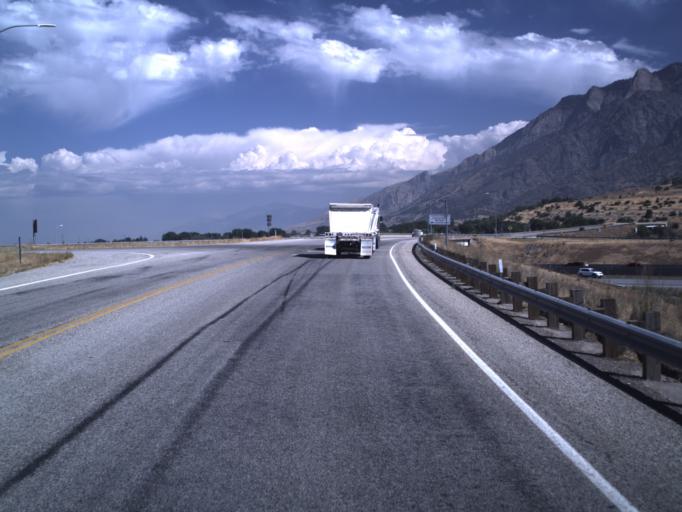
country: US
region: Utah
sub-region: Box Elder County
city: South Willard
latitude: 41.3391
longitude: -112.0375
